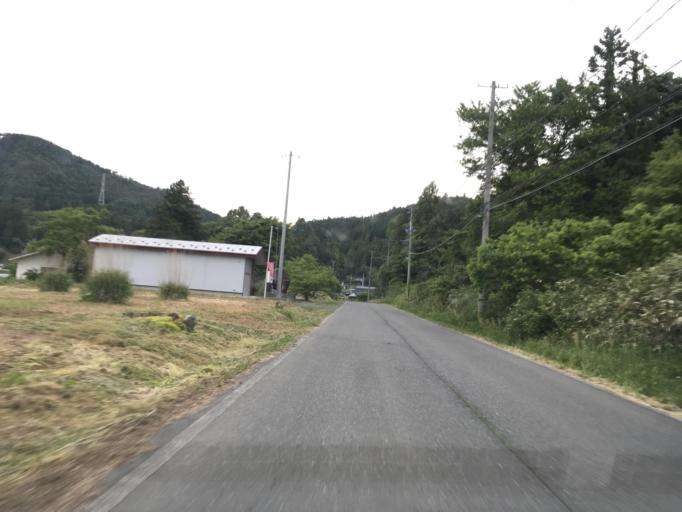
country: JP
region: Iwate
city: Mizusawa
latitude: 39.1776
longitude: 141.2922
